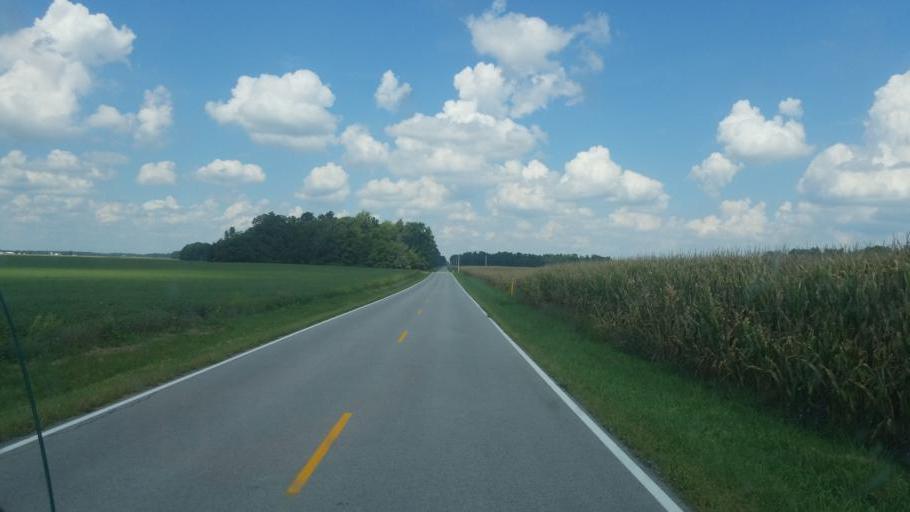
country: US
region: Ohio
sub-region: Hancock County
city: Arlington
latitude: 40.8383
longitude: -83.7277
